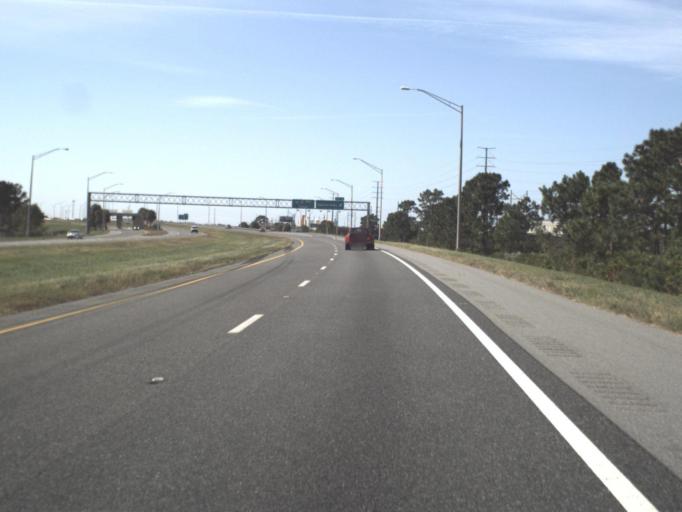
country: US
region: Florida
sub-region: Osceola County
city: Celebration
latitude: 28.3468
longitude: -81.5114
